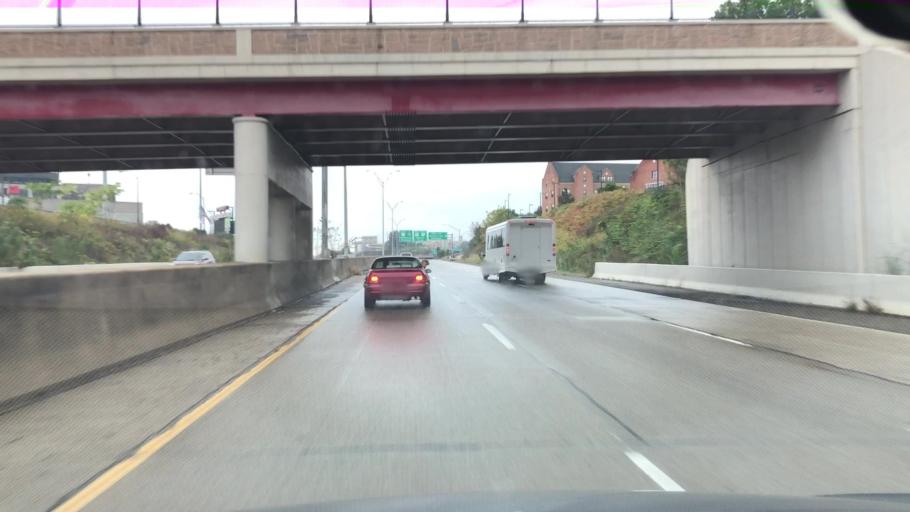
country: US
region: Ohio
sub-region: Mahoning County
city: Youngstown
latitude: 41.1094
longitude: -80.6461
